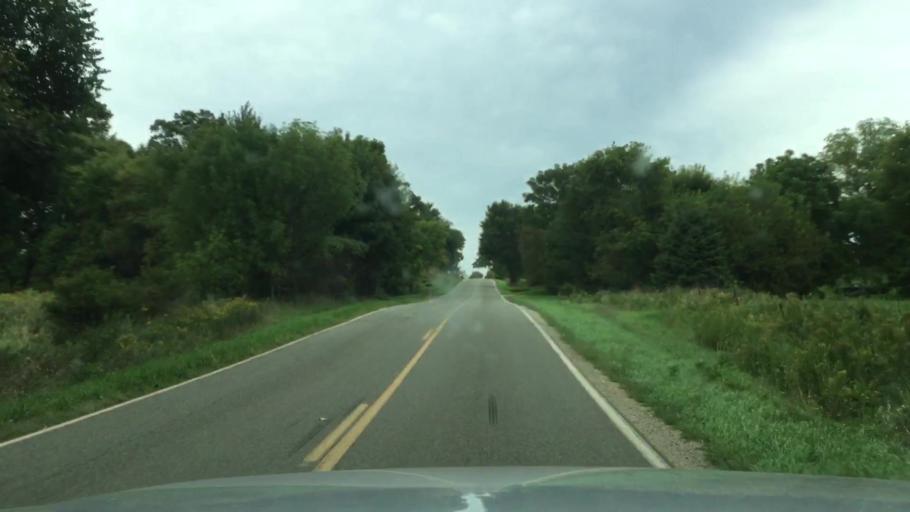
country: US
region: Michigan
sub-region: Shiawassee County
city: Durand
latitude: 42.8229
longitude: -83.9999
